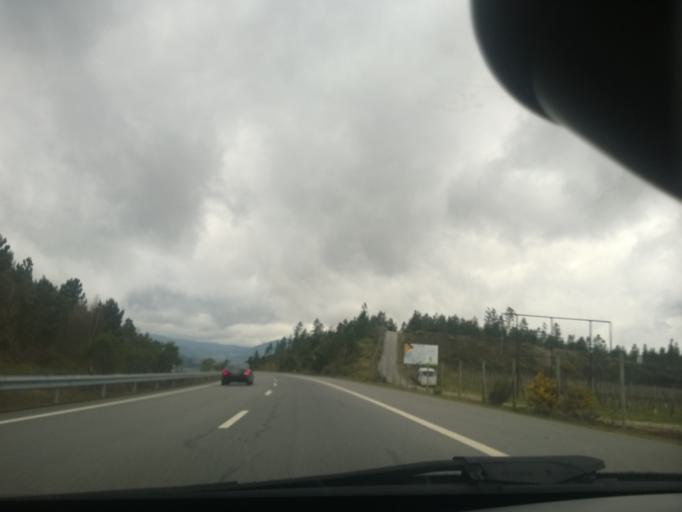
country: PT
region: Braga
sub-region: Cabeceiras de Basto
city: Cabeceiras de Basto
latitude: 41.4818
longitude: -7.9197
